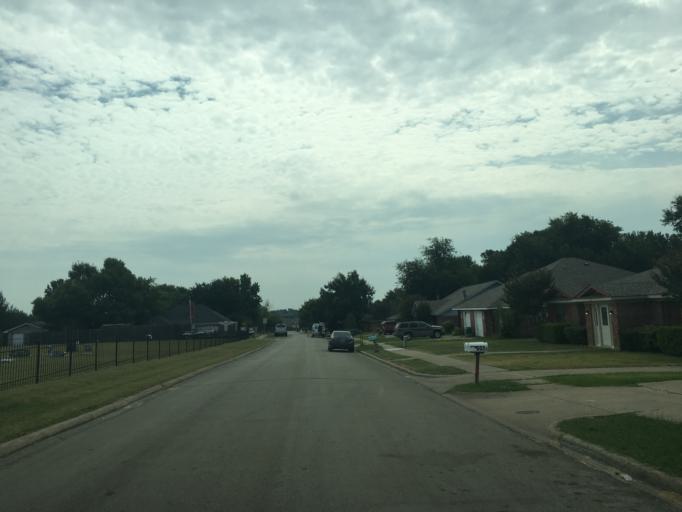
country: US
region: Texas
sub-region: Collin County
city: Wylie
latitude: 33.0139
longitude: -96.5320
